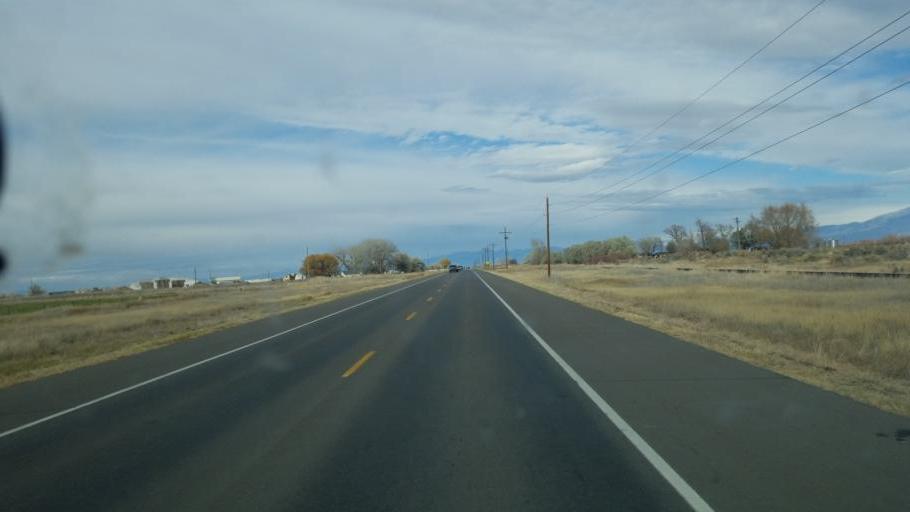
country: US
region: Colorado
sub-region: Alamosa County
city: Alamosa
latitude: 37.3783
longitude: -105.9180
